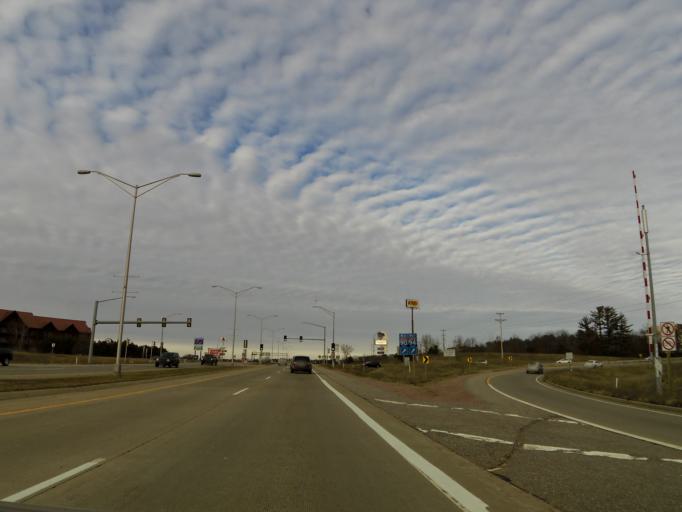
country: US
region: Wisconsin
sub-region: Sauk County
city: Lake Delton
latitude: 43.5705
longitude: -89.7783
